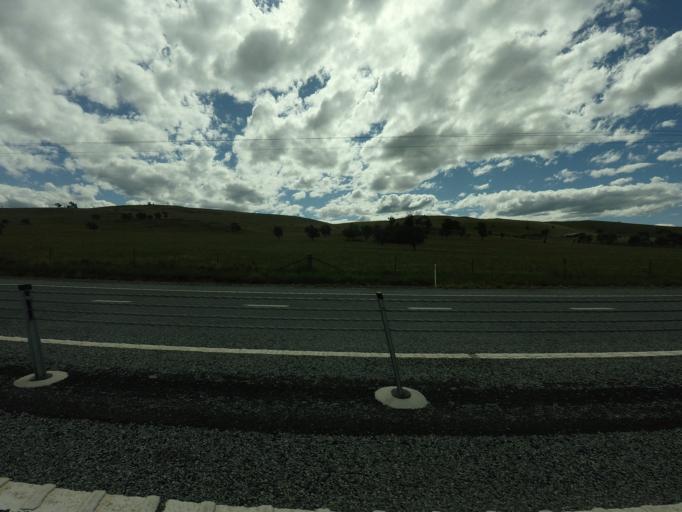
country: AU
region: Tasmania
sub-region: Northern Midlands
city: Evandale
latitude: -42.1166
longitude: 147.4409
